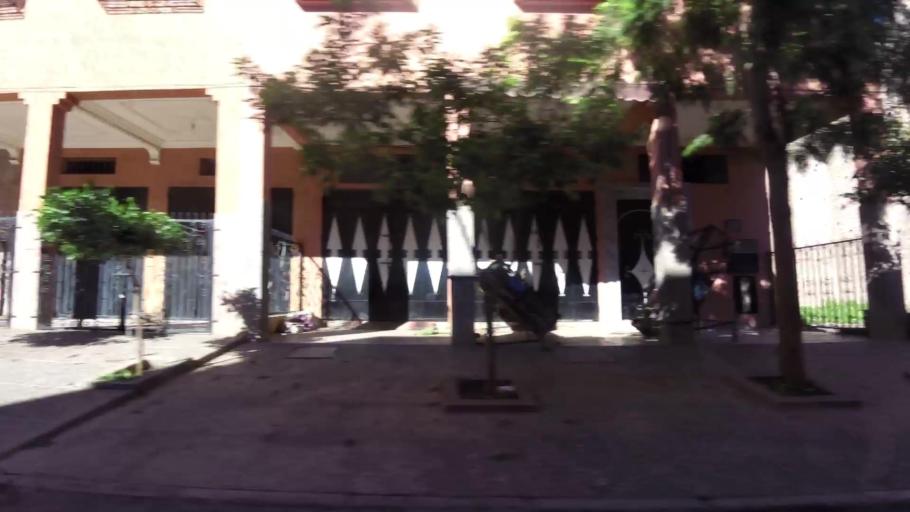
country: MA
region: Marrakech-Tensift-Al Haouz
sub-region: Marrakech
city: Marrakesh
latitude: 31.5988
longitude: -8.0424
